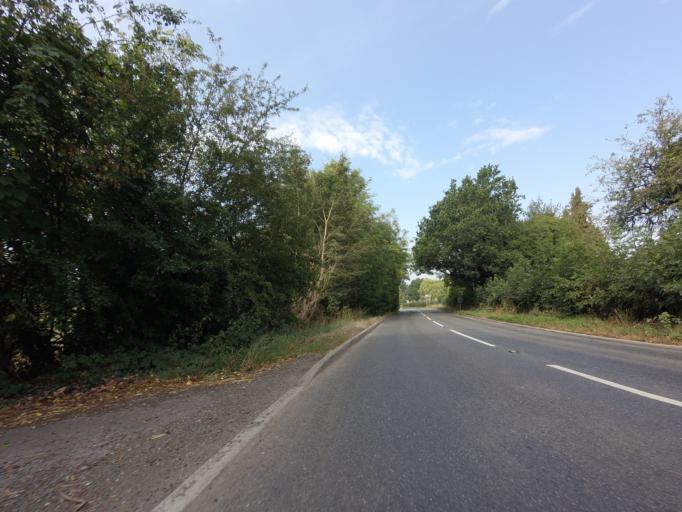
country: GB
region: England
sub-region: Kent
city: Headcorn
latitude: 51.1146
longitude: 0.6406
